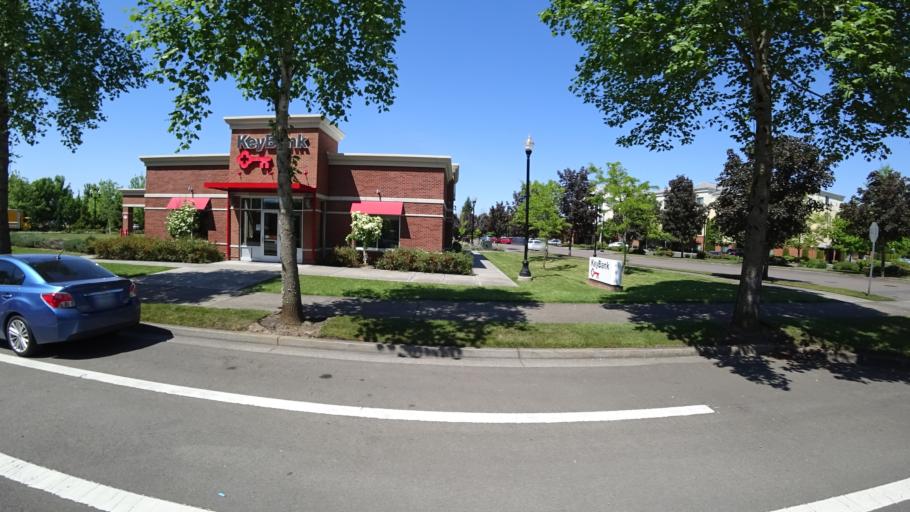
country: US
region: Oregon
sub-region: Washington County
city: Rockcreek
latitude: 45.5373
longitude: -122.9026
